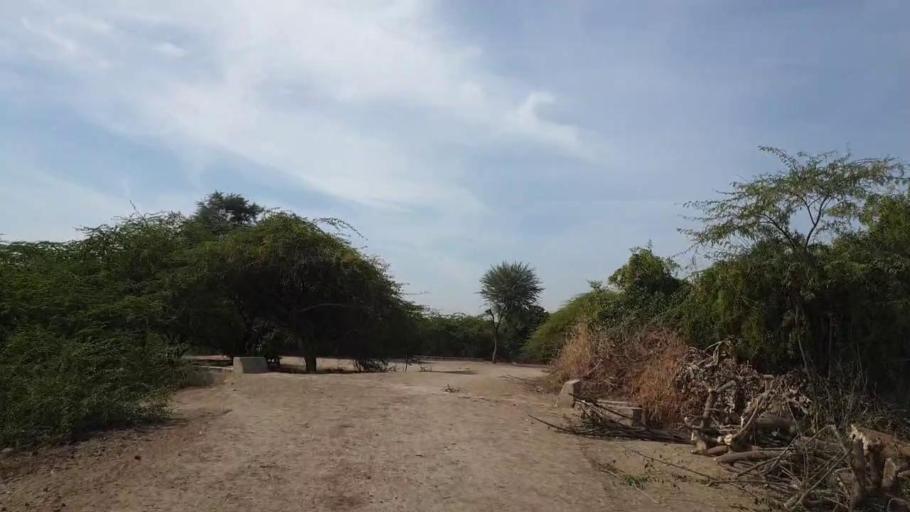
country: PK
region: Sindh
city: Kunri
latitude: 25.1626
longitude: 69.6172
